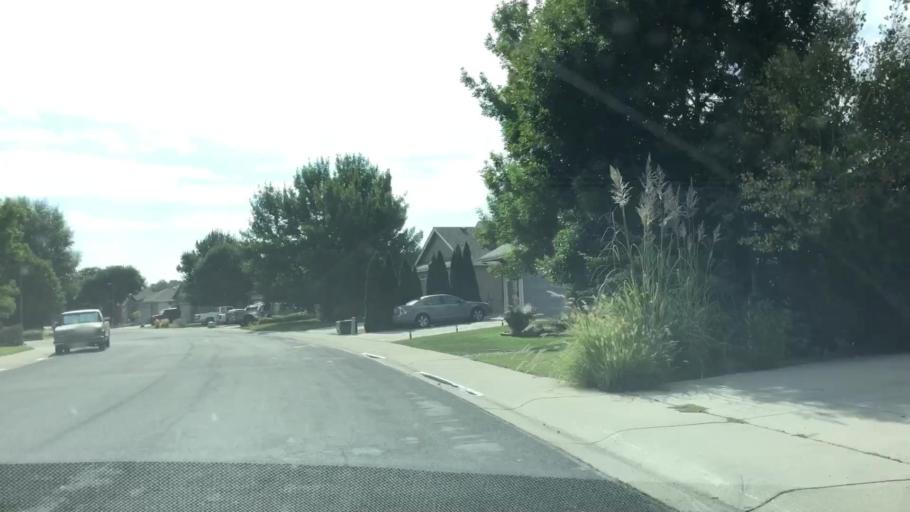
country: US
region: Colorado
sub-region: Larimer County
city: Loveland
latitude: 40.4302
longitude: -105.0567
